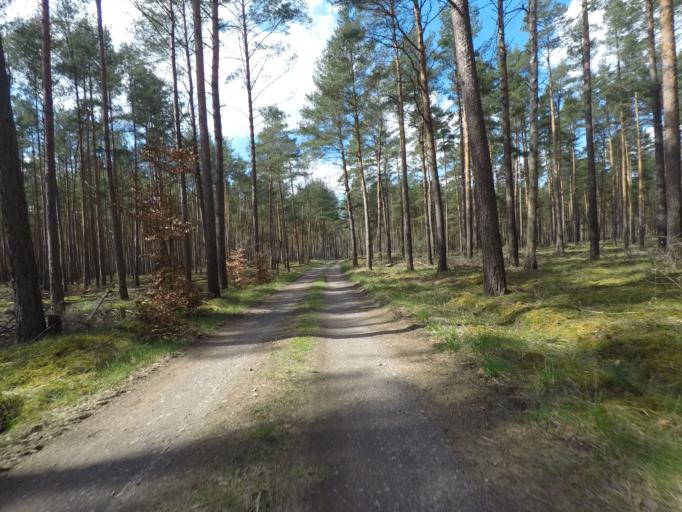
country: DE
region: Brandenburg
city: Melchow
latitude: 52.8192
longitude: 13.6898
